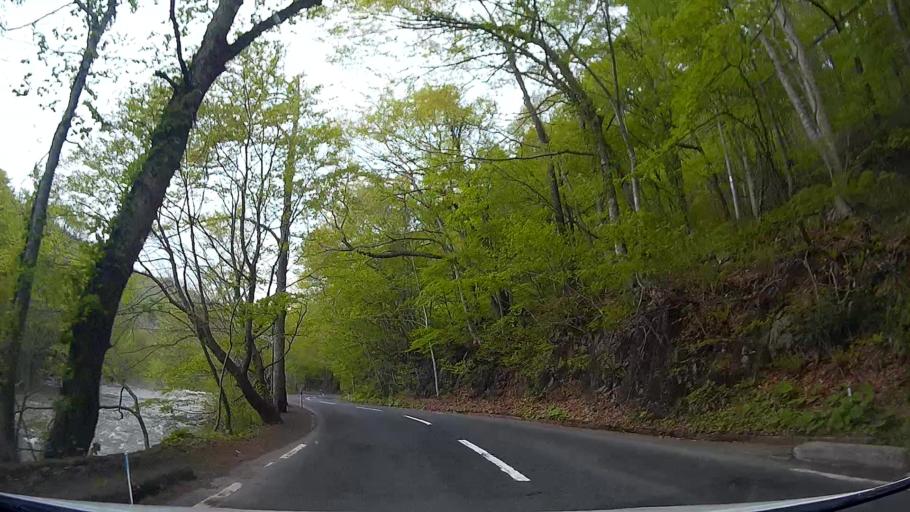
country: JP
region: Aomori
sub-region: Aomori Shi
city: Furudate
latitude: 40.5701
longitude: 140.9793
